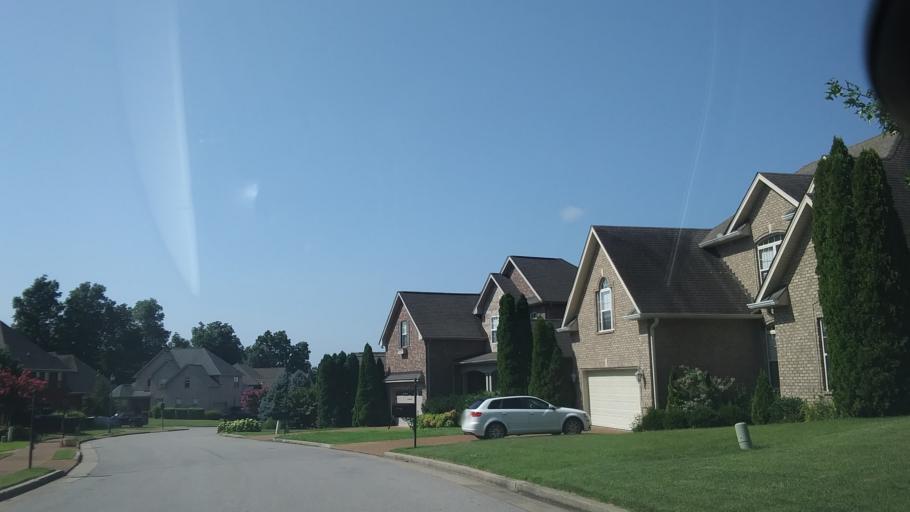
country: US
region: Tennessee
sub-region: Davidson County
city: Belle Meade
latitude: 36.0810
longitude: -86.9219
